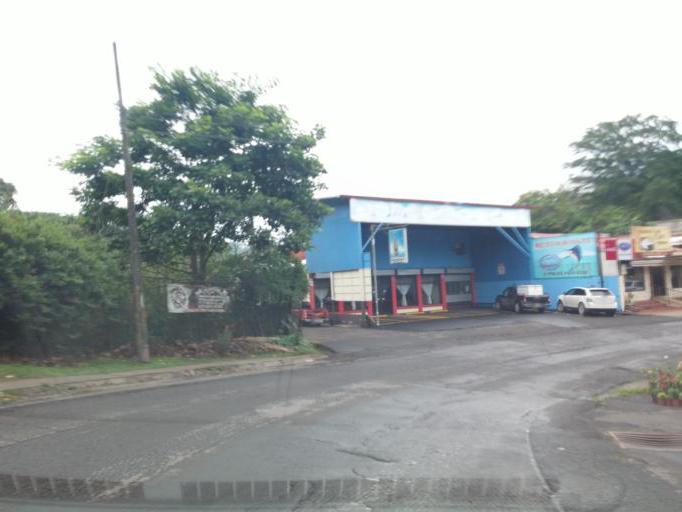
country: CR
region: Alajuela
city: San Juan
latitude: 10.0877
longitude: -84.3419
